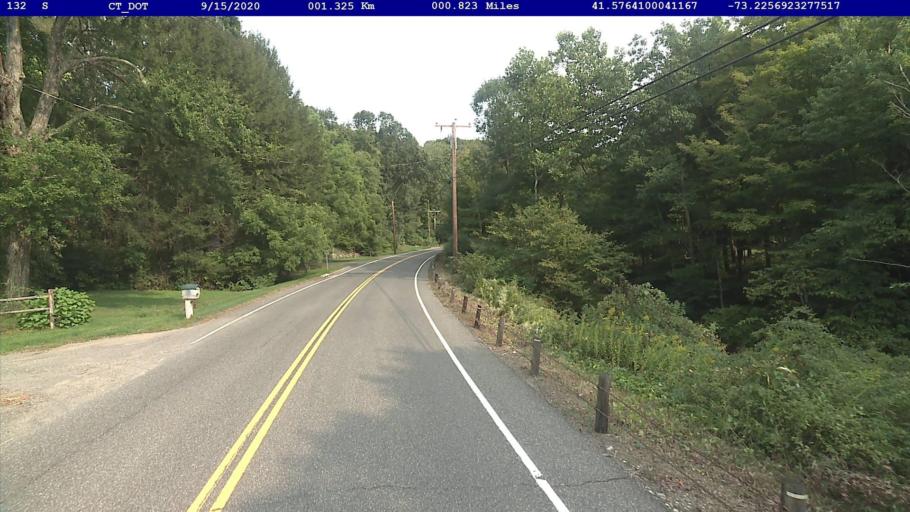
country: US
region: Connecticut
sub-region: Litchfield County
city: Woodbury
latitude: 41.5764
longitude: -73.2257
